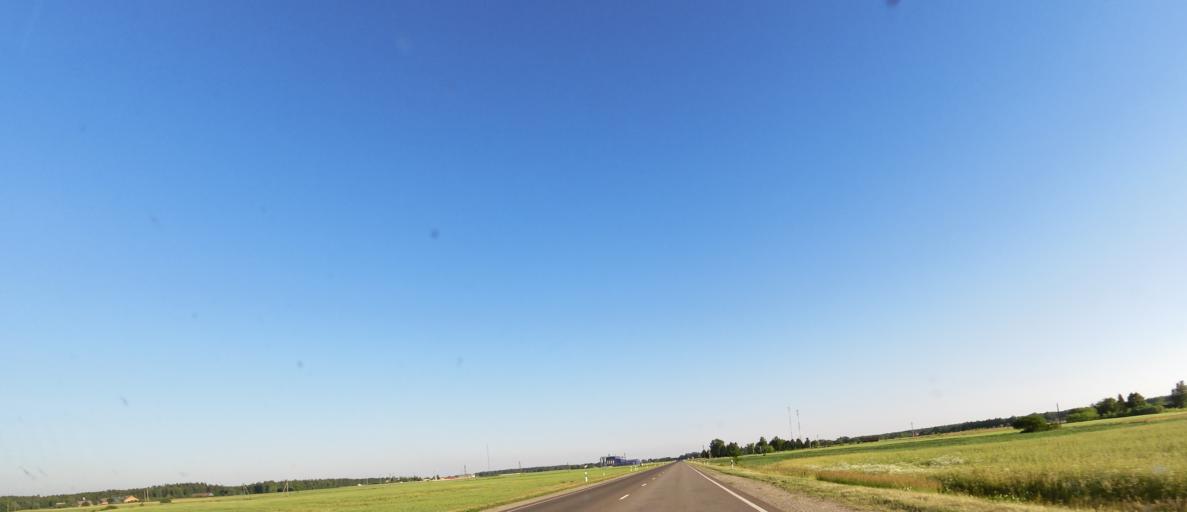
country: LT
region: Panevezys
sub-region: Panevezys City
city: Panevezys
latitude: 55.7988
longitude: 24.3690
